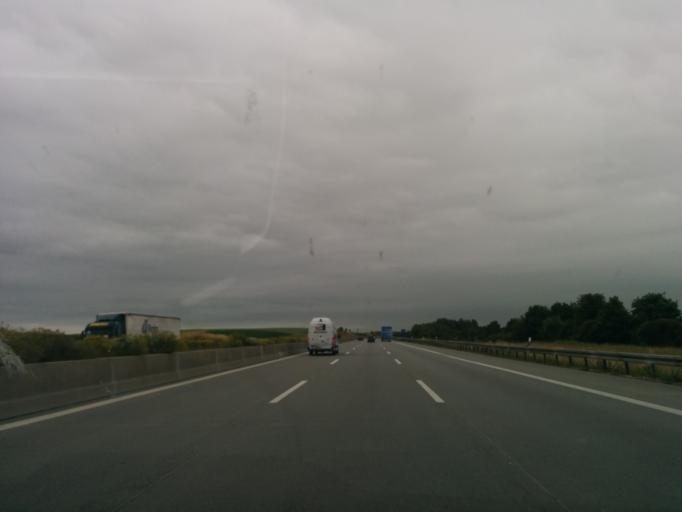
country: DE
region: Bavaria
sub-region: Swabia
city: Dasing
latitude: 48.3963
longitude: 11.0461
